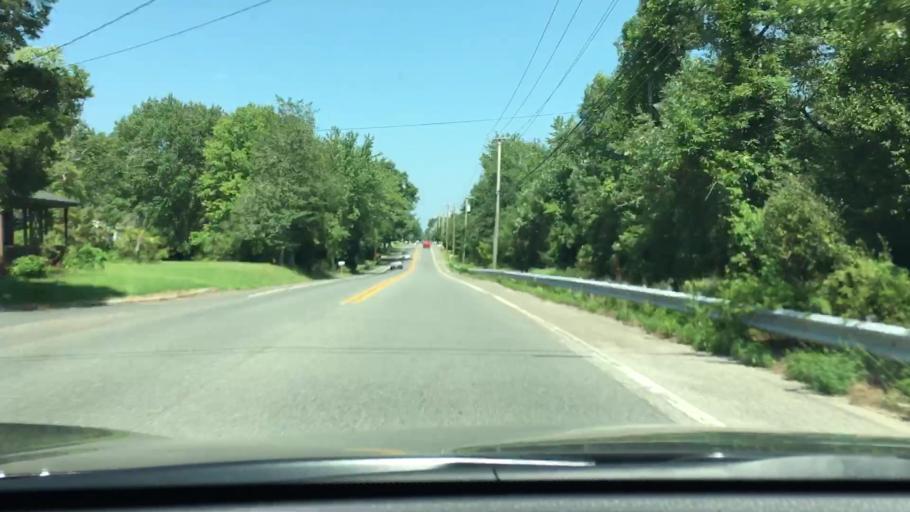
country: US
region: New Jersey
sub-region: Cumberland County
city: Laurel Lake
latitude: 39.3155
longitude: -75.0106
